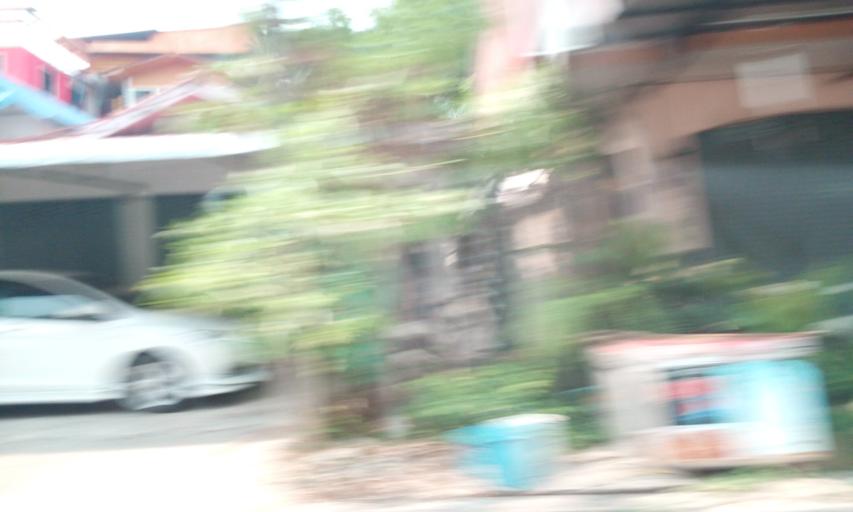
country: TH
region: Chiang Rai
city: Chiang Rai
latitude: 19.9115
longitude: 99.8244
